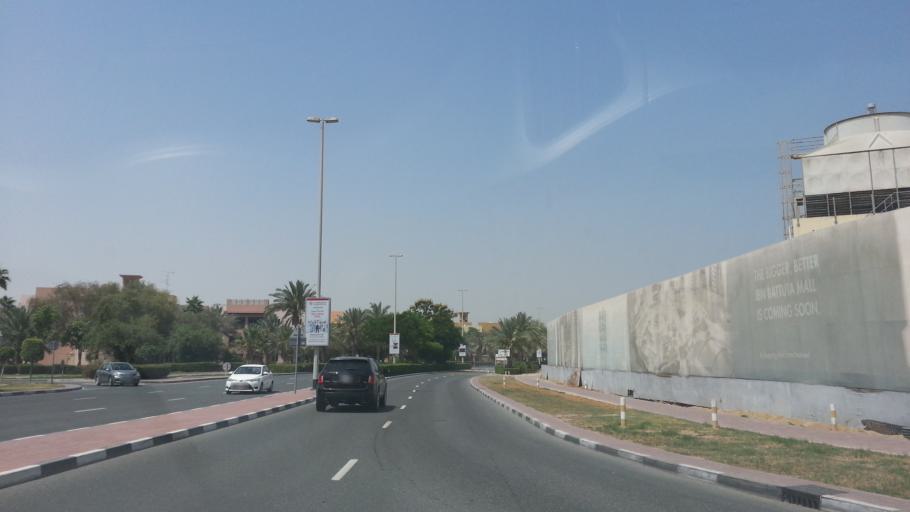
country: AE
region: Dubai
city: Dubai
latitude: 25.0478
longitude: 55.1287
